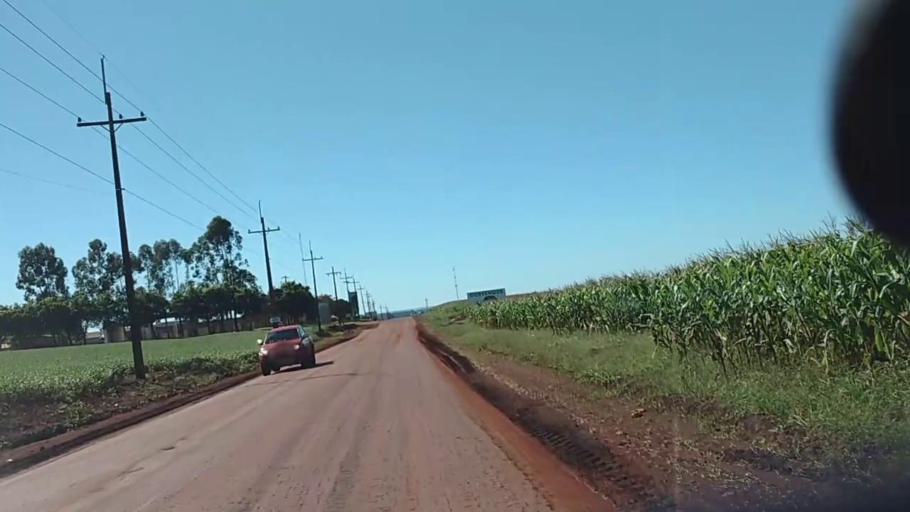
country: PY
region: Alto Parana
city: Naranjal
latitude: -25.9747
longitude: -55.2146
